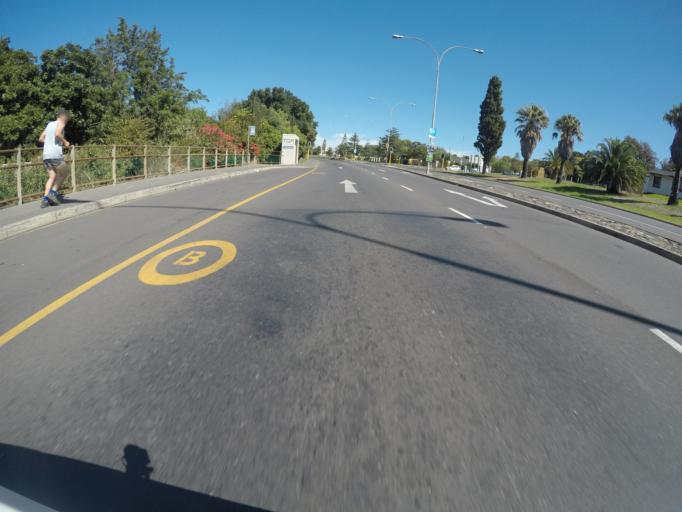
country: ZA
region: Western Cape
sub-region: City of Cape Town
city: Kraaifontein
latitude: -33.8447
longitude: 18.6454
